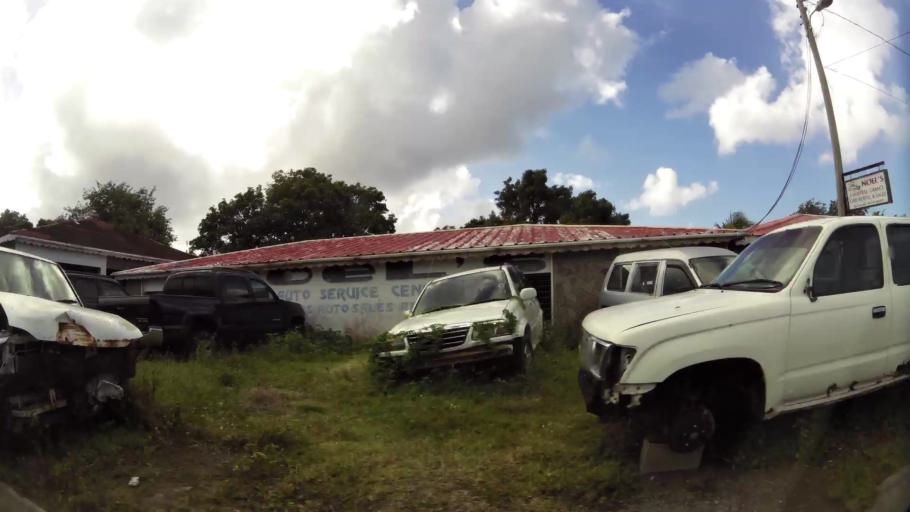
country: KN
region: Saint Paul Charlestown
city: Charlestown
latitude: 17.1285
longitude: -62.6116
